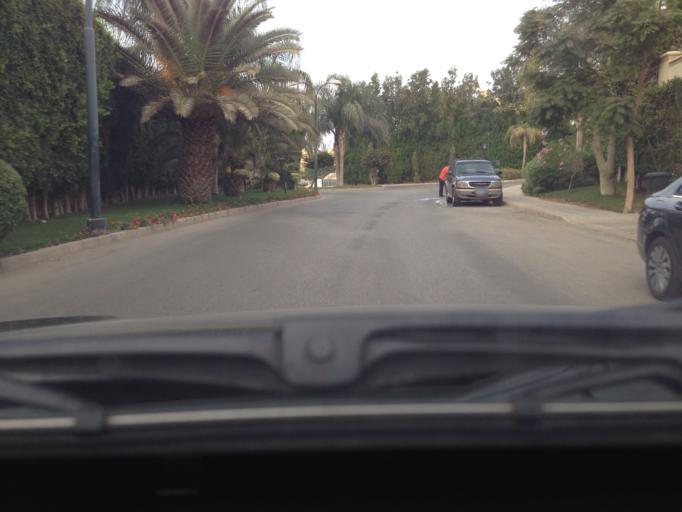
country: EG
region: Muhafazat al Qahirah
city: Cairo
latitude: 29.9954
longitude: 31.3994
